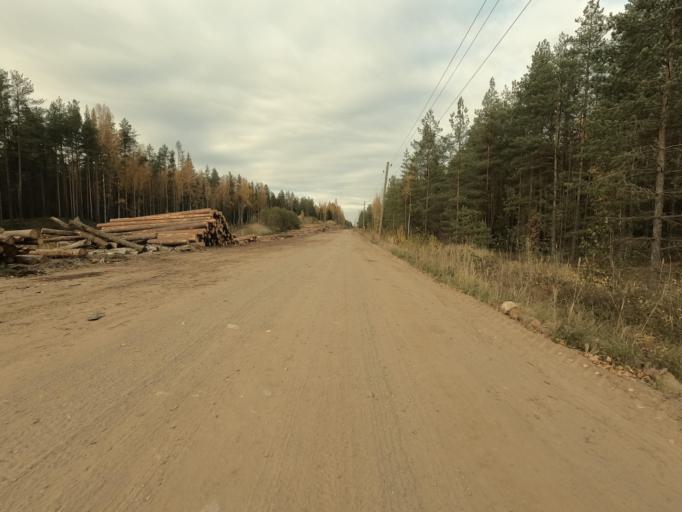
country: RU
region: Leningrad
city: Priladozhskiy
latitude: 59.6904
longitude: 31.3608
